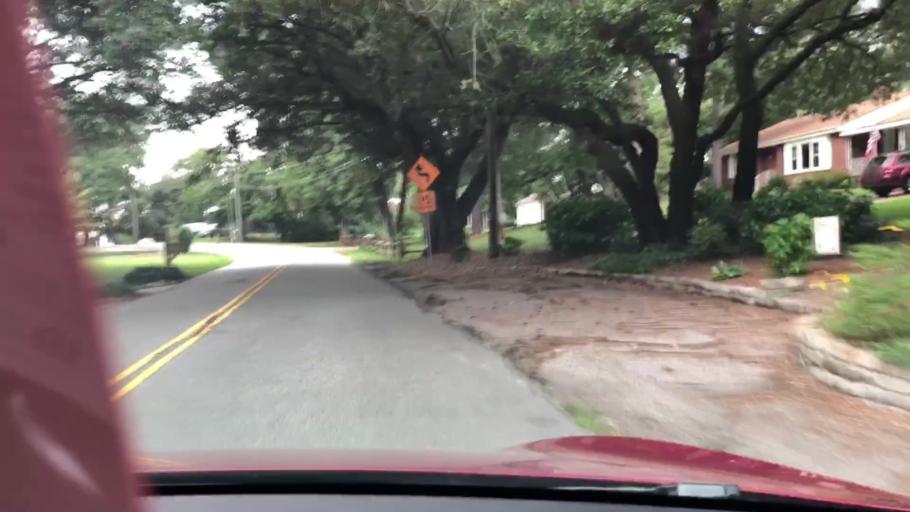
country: US
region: Virginia
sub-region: City of Virginia Beach
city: Virginia Beach
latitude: 36.9068
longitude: -76.0805
